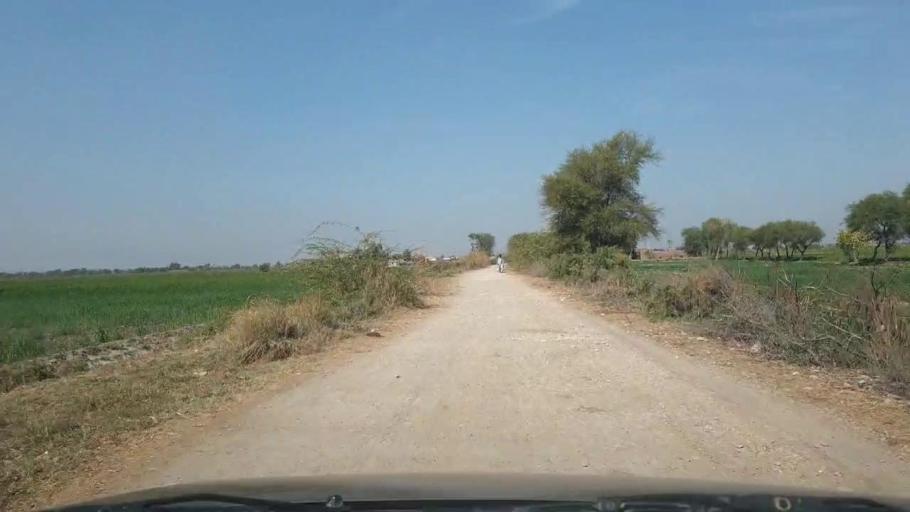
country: PK
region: Sindh
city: Mirpur Khas
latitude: 25.4392
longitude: 69.1646
